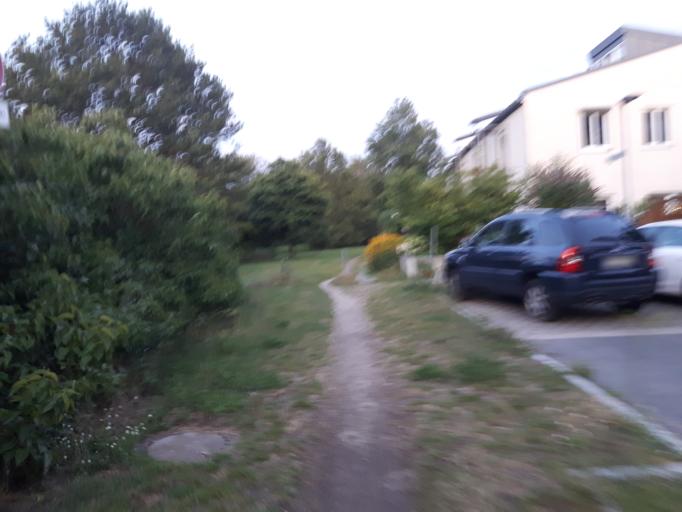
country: DE
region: Berlin
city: Staaken
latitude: 52.5610
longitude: 13.1394
